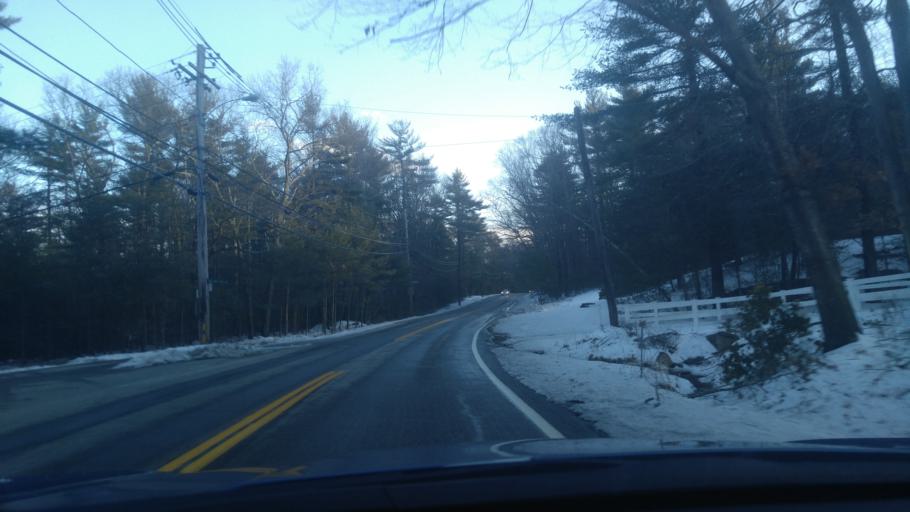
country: US
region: Rhode Island
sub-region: Kent County
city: West Greenwich
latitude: 41.6849
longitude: -71.6175
